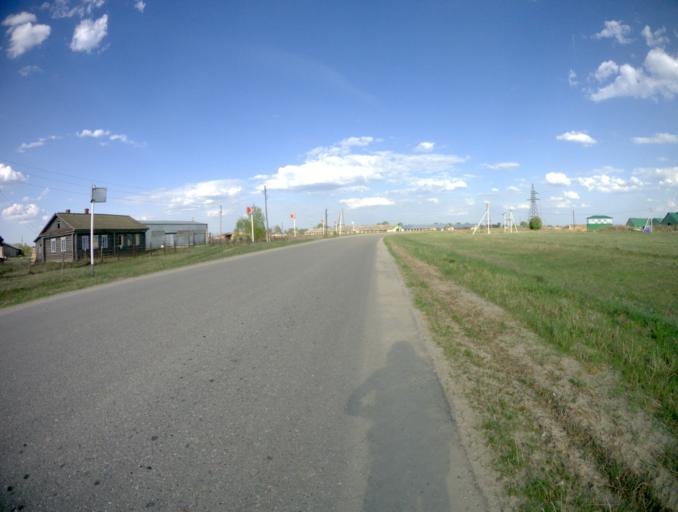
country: RU
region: Ivanovo
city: Kolobovo
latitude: 56.5443
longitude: 41.5441
